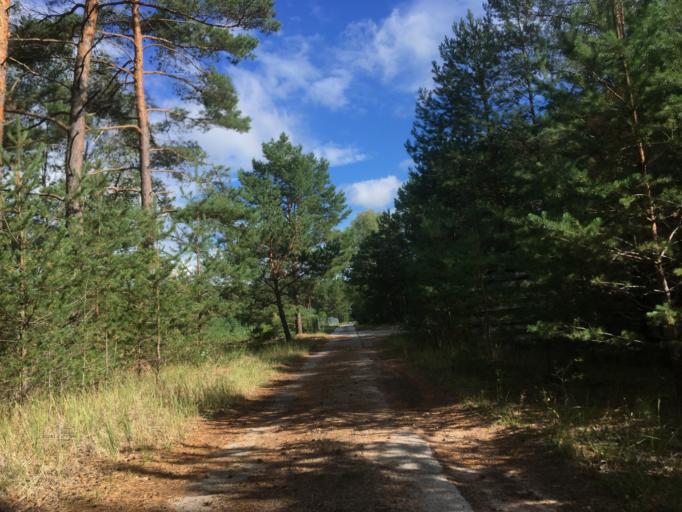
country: DE
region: Brandenburg
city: Halbe
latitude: 52.1683
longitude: 13.7500
